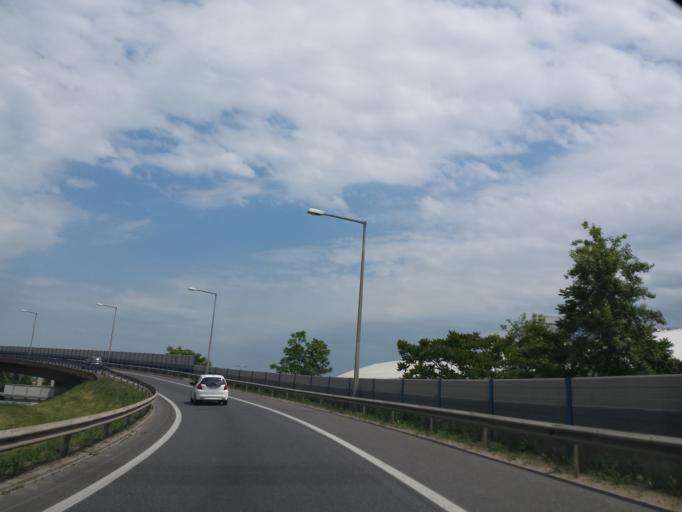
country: AT
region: Vienna
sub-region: Wien Stadt
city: Vienna
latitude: 48.1809
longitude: 16.4029
